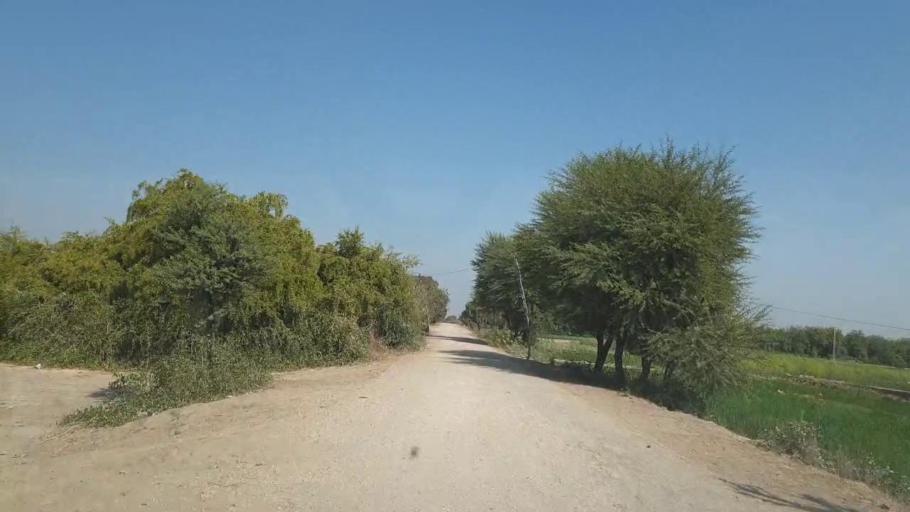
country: PK
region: Sindh
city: Mirpur Khas
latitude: 25.6661
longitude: 69.1103
